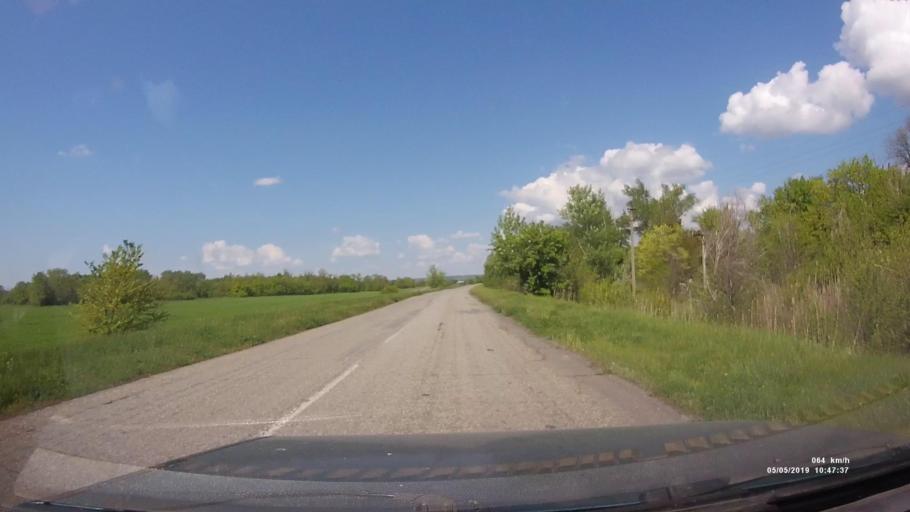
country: RU
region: Rostov
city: Ust'-Donetskiy
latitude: 47.6392
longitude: 40.8303
